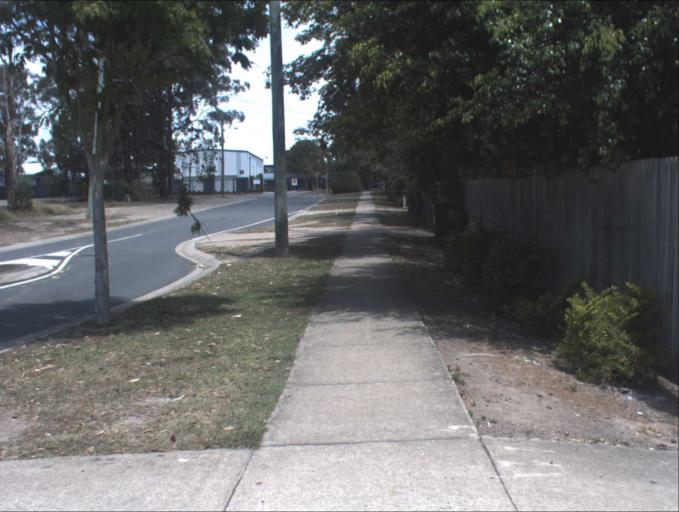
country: AU
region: Queensland
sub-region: Logan
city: Woodridge
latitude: -27.6408
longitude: 153.0973
